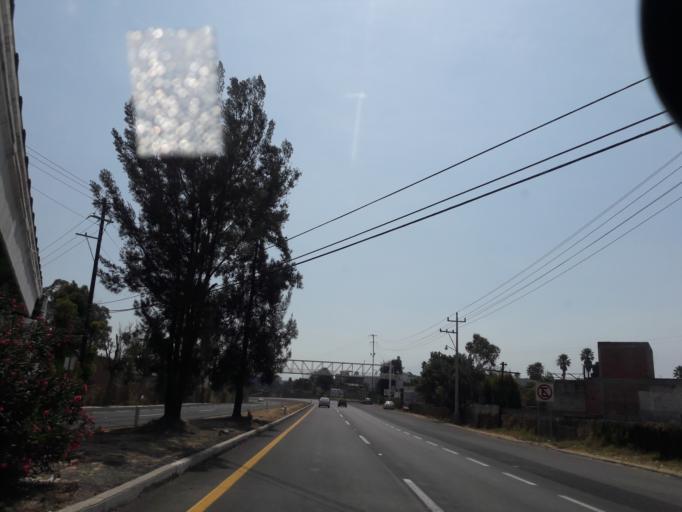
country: MX
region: Tlaxcala
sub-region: Totolac
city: Zaragoza
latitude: 19.3208
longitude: -98.2646
